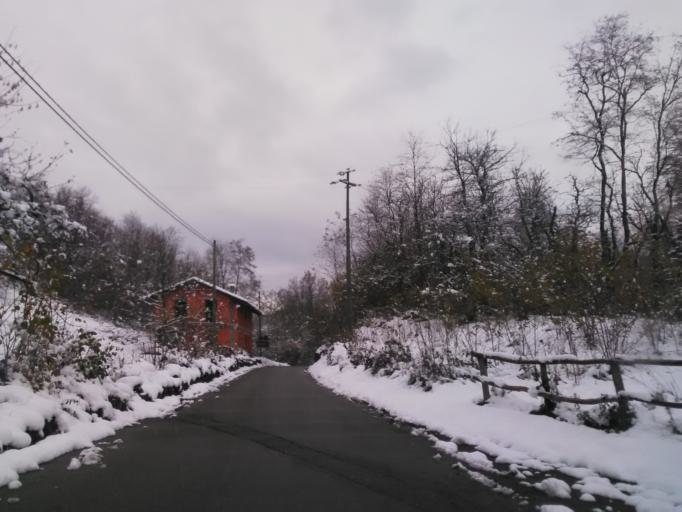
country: IT
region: Piedmont
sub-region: Provincia di Vercelli
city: Varallo
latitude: 45.7968
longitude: 8.2582
